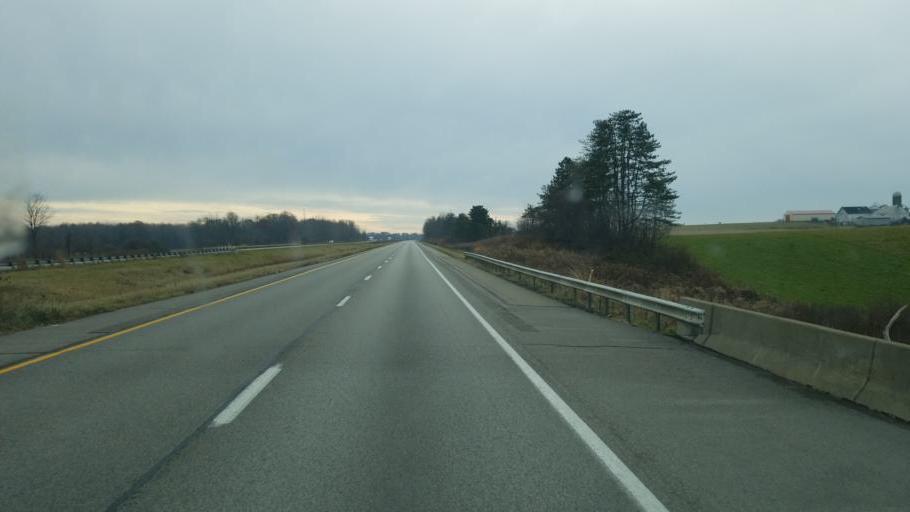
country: US
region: Pennsylvania
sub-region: Mercer County
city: Stoneboro
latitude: 41.3517
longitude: -80.1598
